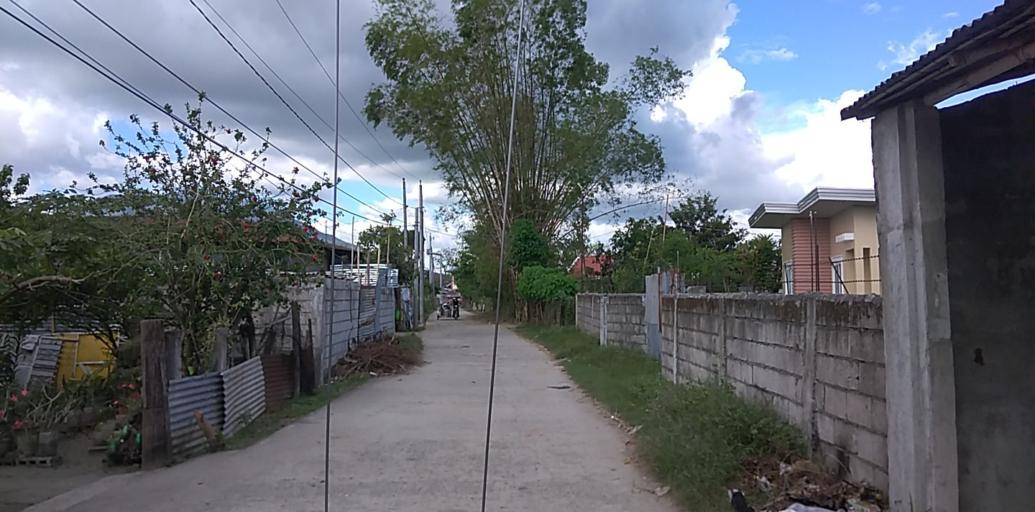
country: PH
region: Central Luzon
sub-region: Province of Pampanga
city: Arayat
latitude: 15.1362
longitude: 120.7822
